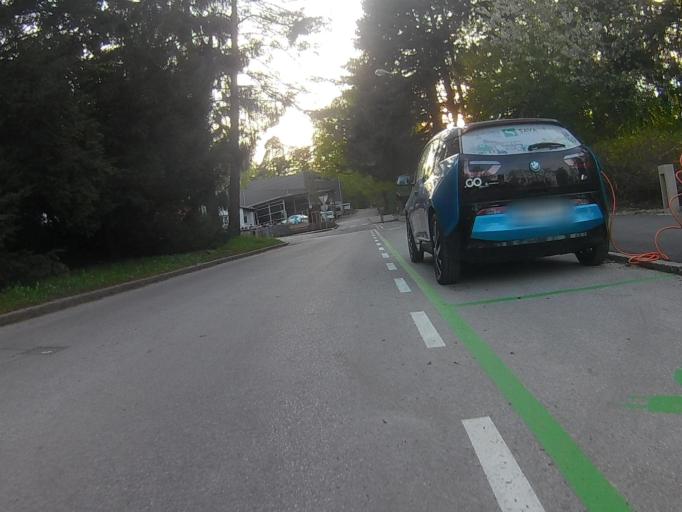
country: SI
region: Maribor
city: Pekre
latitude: 46.5335
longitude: 15.6000
